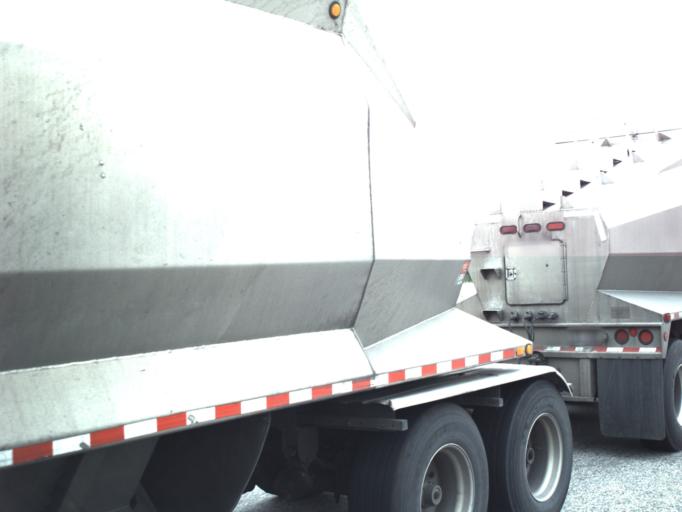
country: US
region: Utah
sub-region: Carbon County
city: Carbonville
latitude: 39.6084
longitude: -110.8337
